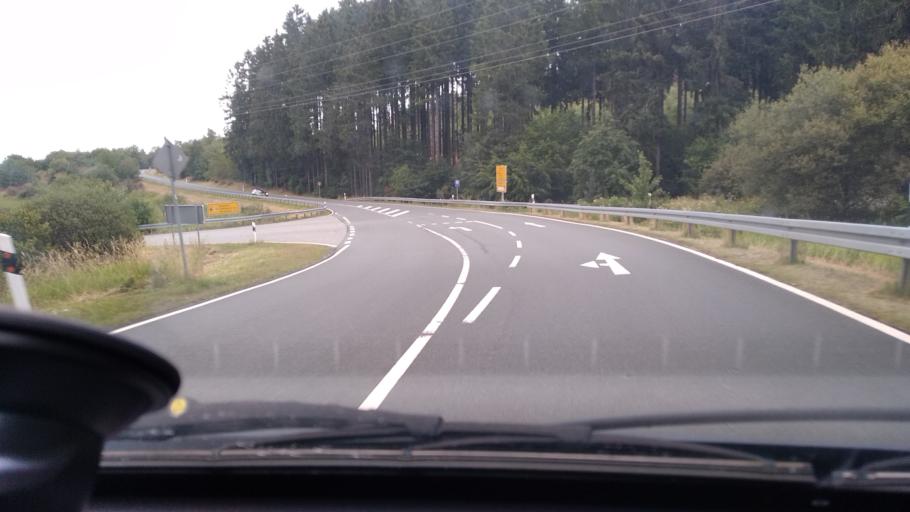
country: DE
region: Hesse
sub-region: Regierungsbezirk Giessen
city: Siegbach
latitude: 50.7888
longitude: 8.3785
